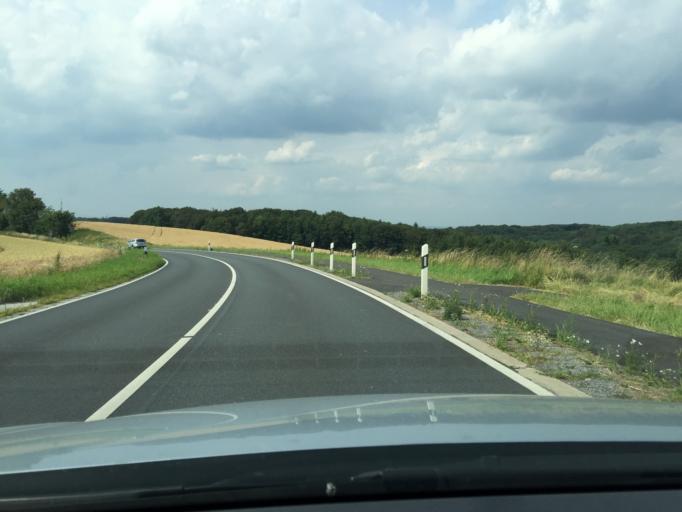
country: DE
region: North Rhine-Westphalia
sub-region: Regierungsbezirk Dusseldorf
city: Velbert
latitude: 51.3568
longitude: 7.0839
